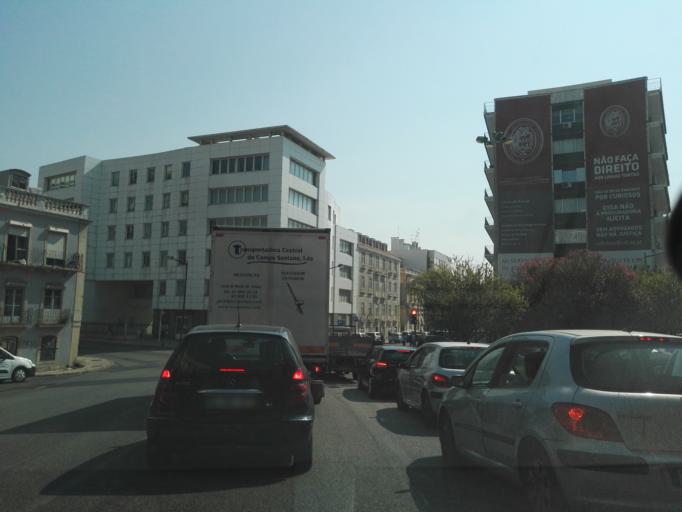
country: PT
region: Lisbon
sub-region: Lisbon
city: Lisbon
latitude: 38.7267
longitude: -9.1367
